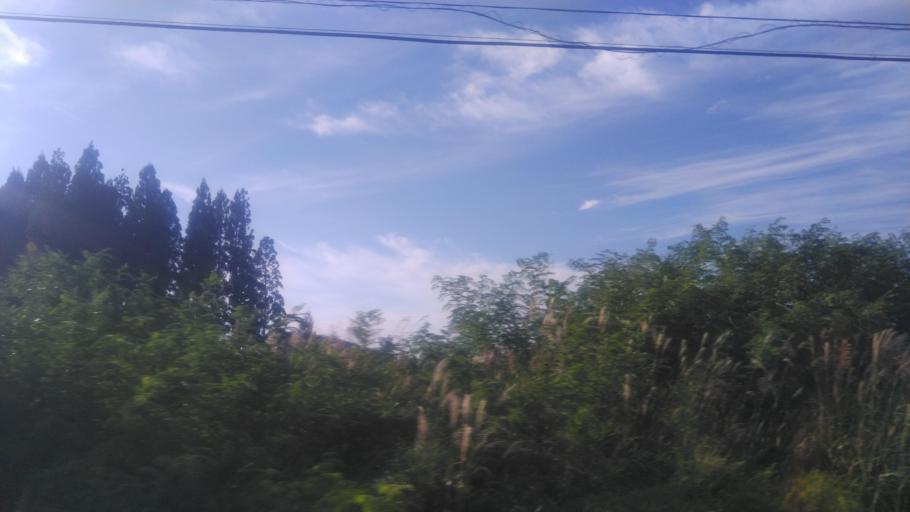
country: JP
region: Akita
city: Takanosu
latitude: 40.2554
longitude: 140.3943
